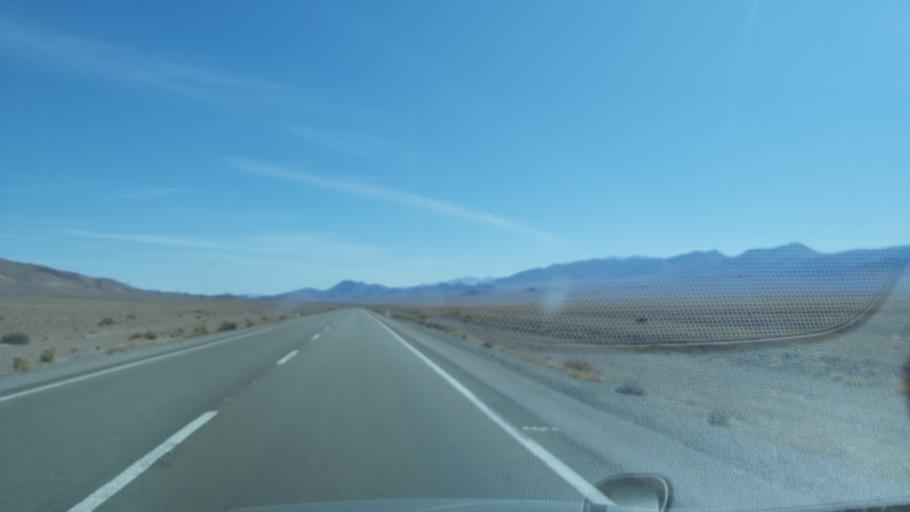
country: CL
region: Atacama
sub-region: Provincia de Chanaral
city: Diego de Almagro
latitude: -26.8724
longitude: -69.9093
